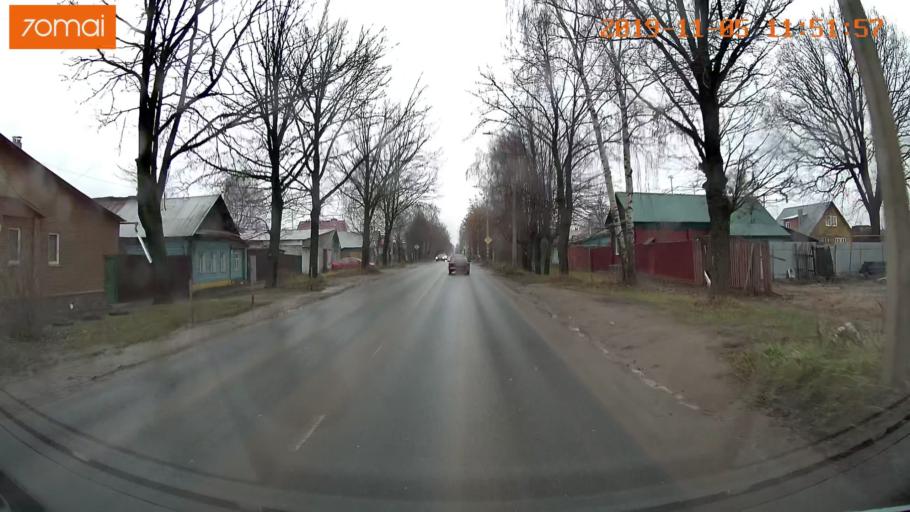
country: RU
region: Ivanovo
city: Bogorodskoye
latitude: 57.0027
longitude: 41.0289
